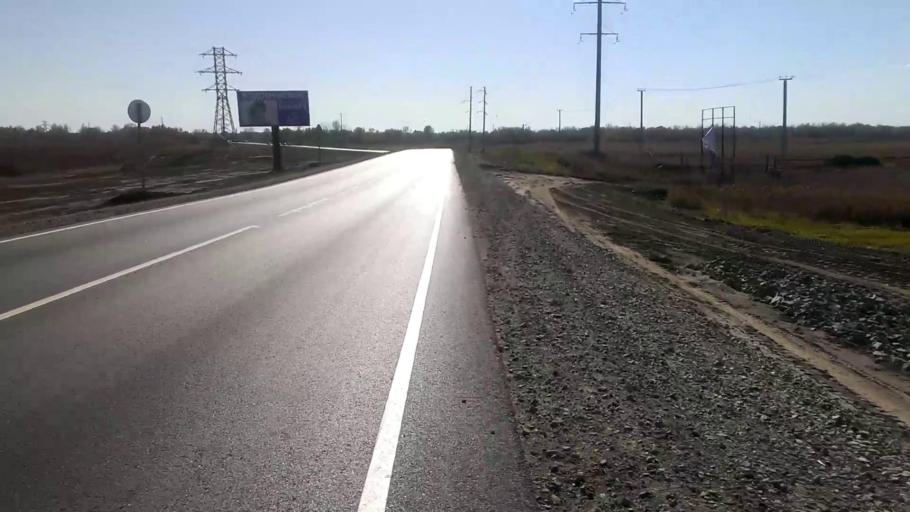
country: RU
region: Altai Krai
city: Sannikovo
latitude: 53.3349
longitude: 83.9382
